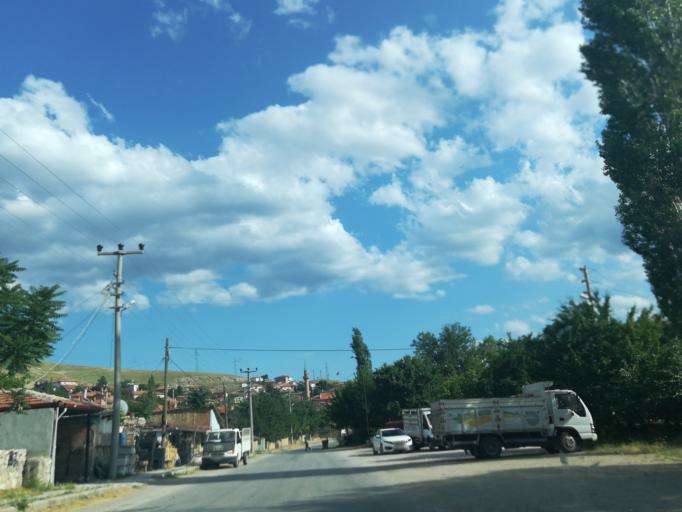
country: TR
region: Afyonkarahisar
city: Dinar
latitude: 38.0775
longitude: 30.1687
